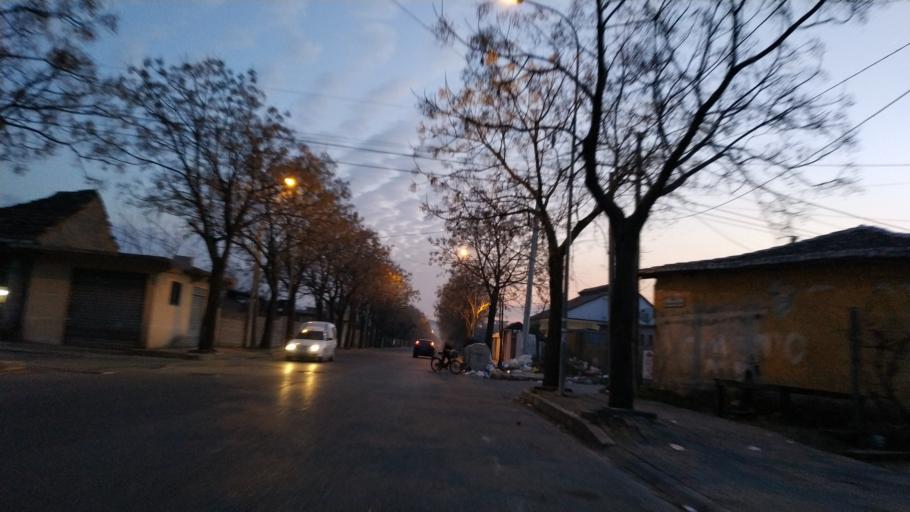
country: AL
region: Shkoder
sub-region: Rrethi i Shkodres
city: Shkoder
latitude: 42.0740
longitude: 19.5025
